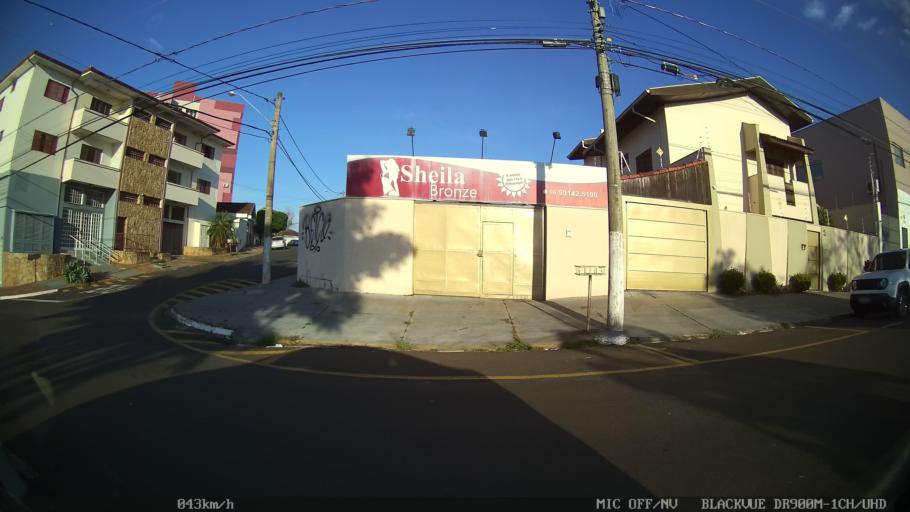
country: BR
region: Sao Paulo
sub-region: Franca
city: Franca
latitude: -20.5218
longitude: -47.3857
